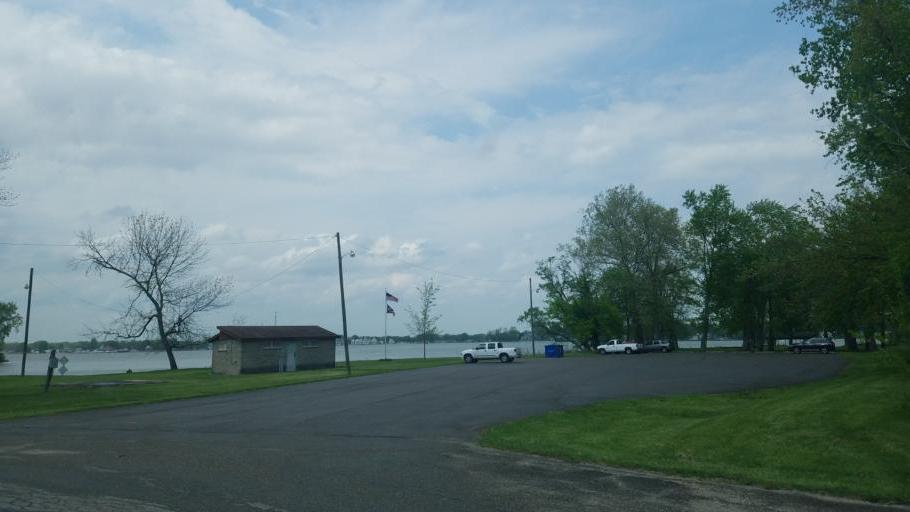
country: US
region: Ohio
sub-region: Fairfield County
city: Fairfield Beach
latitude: 39.9219
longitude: -82.4696
